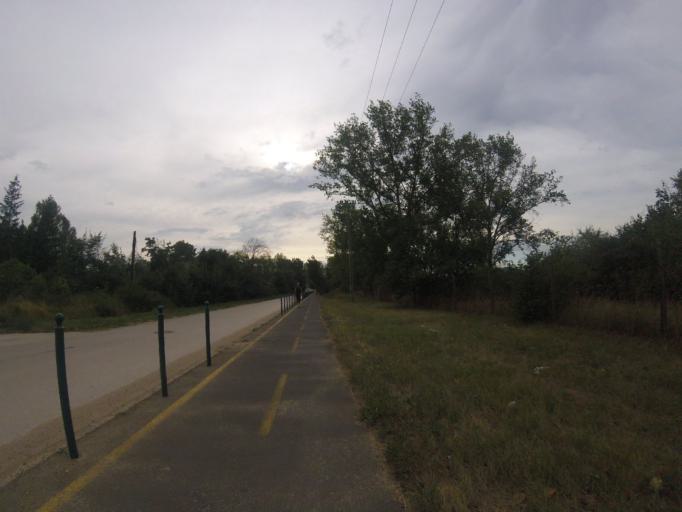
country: HU
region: Pest
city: Budakalasz
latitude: 47.6190
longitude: 19.0739
